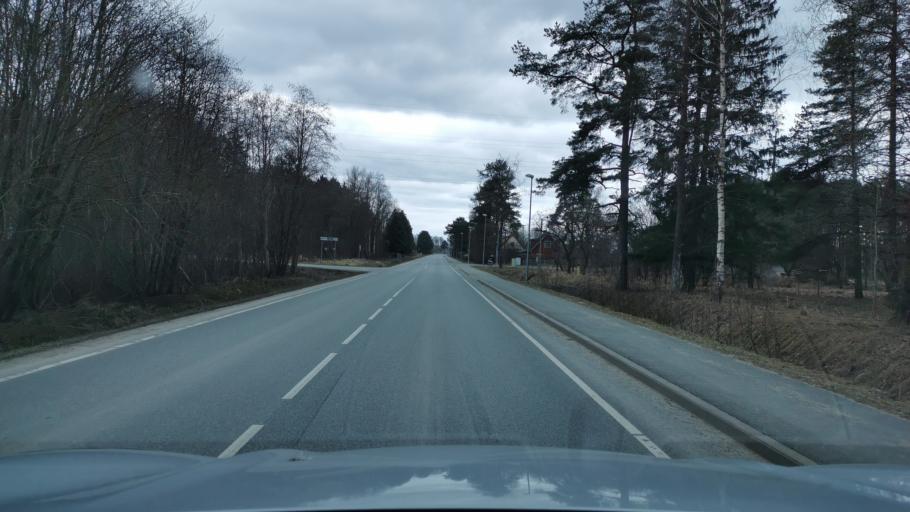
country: EE
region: Ida-Virumaa
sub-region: Puessi linn
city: Pussi
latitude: 59.3648
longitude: 27.0484
